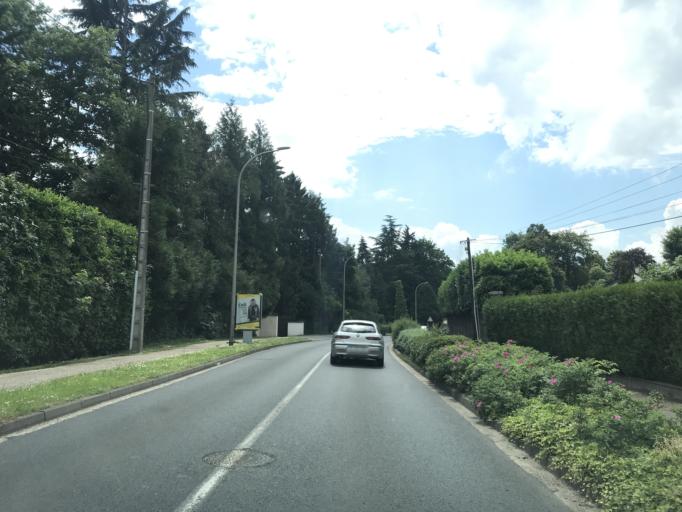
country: FR
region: Haute-Normandie
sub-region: Departement de la Seine-Maritime
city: Mont-Saint-Aignan
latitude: 49.4666
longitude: 1.0890
